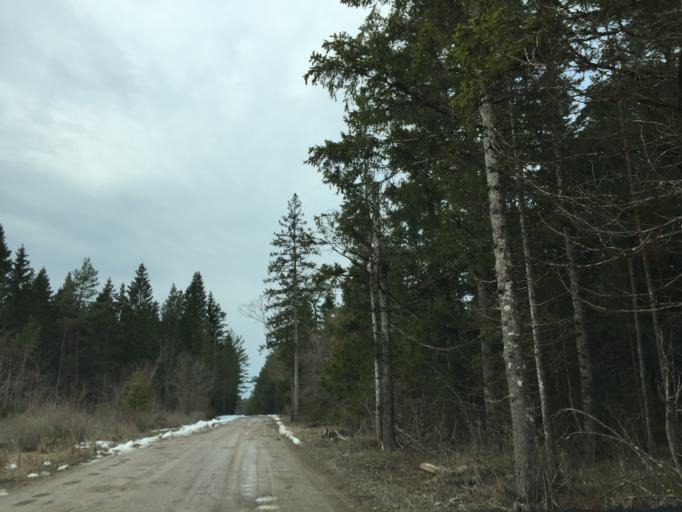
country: EE
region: Saare
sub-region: Kuressaare linn
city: Kuressaare
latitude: 58.4265
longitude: 22.1491
